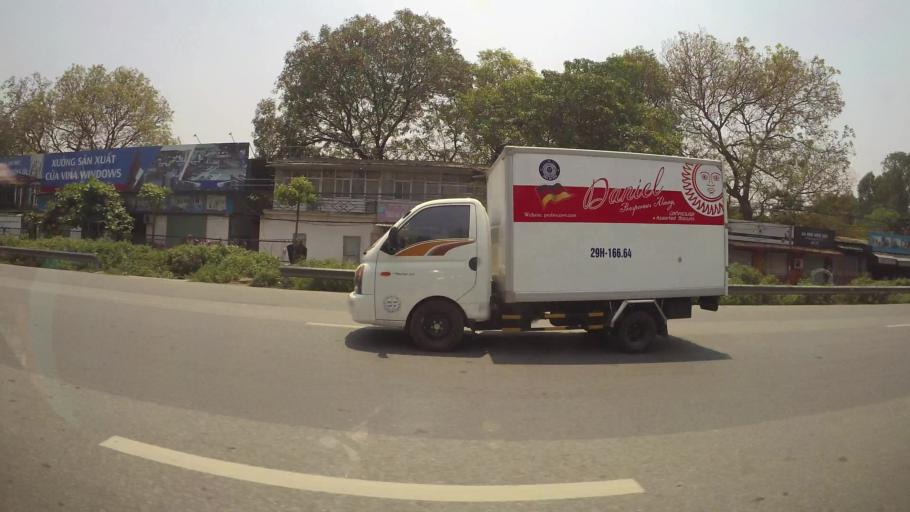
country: VN
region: Ha Noi
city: Trau Quy
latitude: 21.0321
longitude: 105.9095
